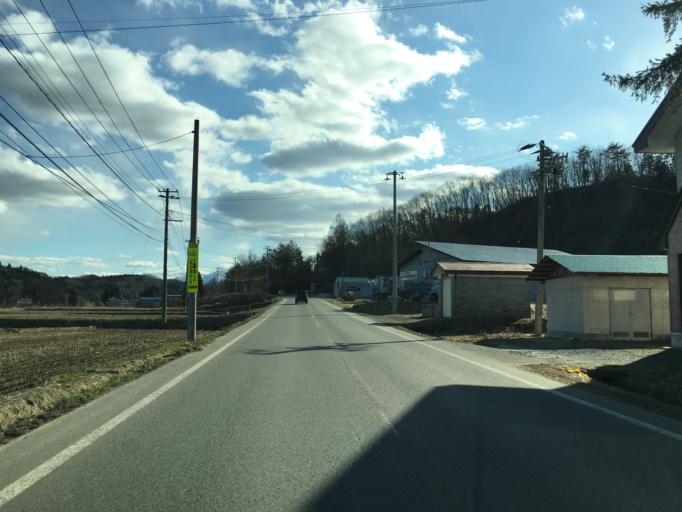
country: JP
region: Yamagata
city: Nagai
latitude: 37.9889
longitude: 140.0040
